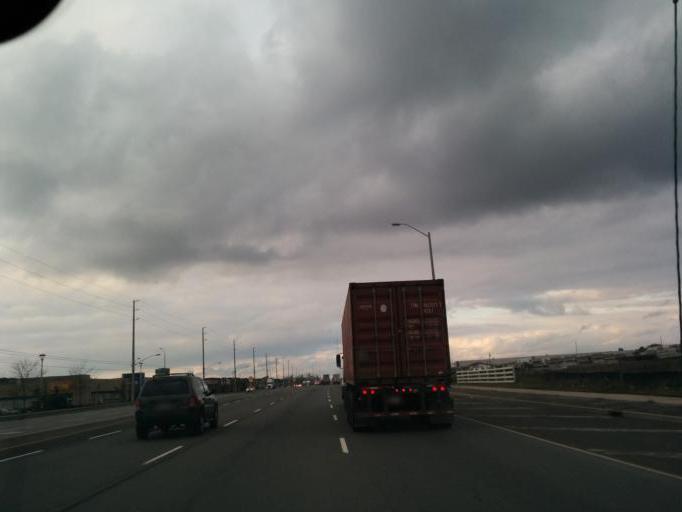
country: CA
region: Ontario
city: Brampton
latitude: 43.7749
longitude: -79.6528
